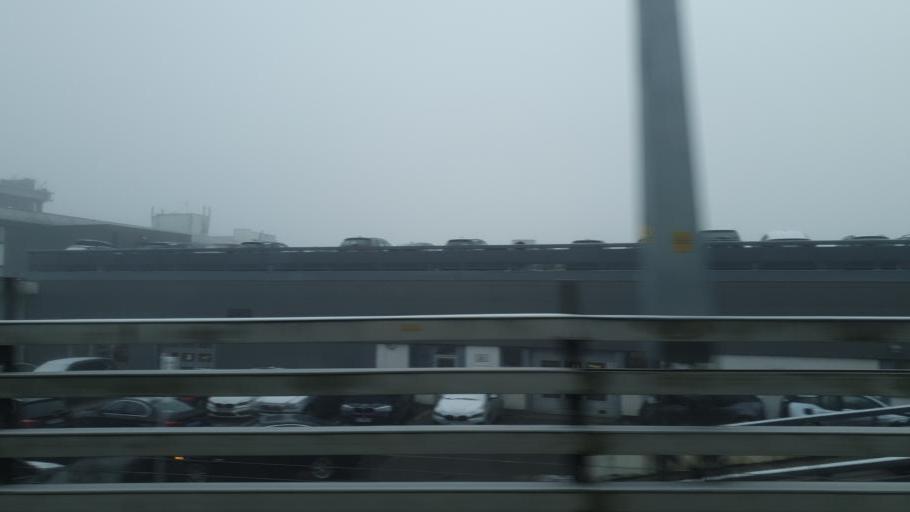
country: NO
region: Oslo
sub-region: Oslo
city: Sjolyststranda
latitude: 59.9183
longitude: 10.6601
